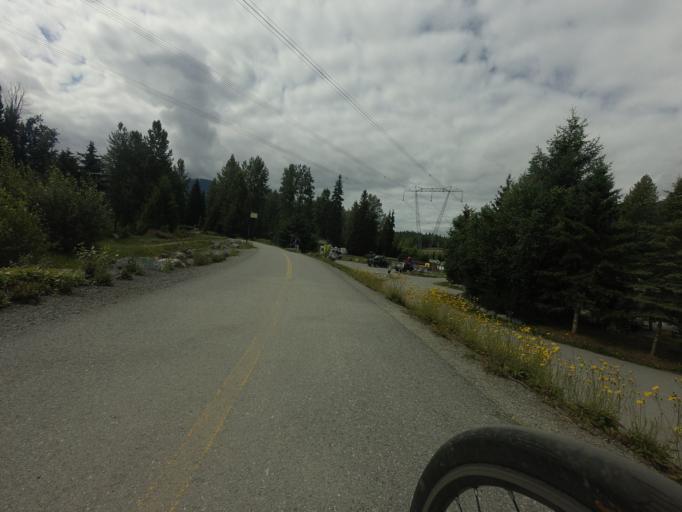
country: CA
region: British Columbia
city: Whistler
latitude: 50.1371
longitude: -122.9507
